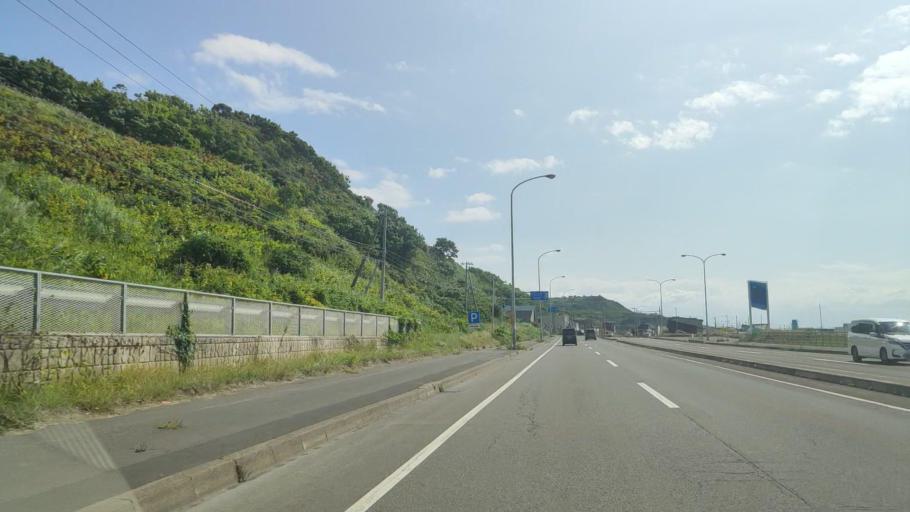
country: JP
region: Hokkaido
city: Rumoi
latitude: 44.0021
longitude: 141.6579
